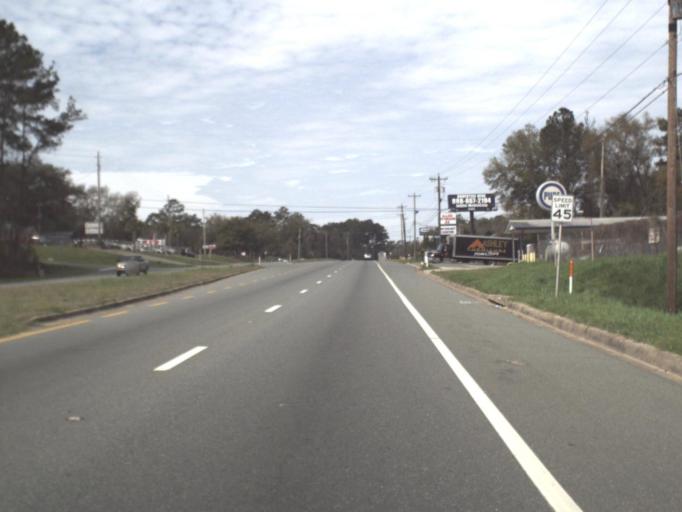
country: US
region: Florida
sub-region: Gadsden County
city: Midway
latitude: 30.4570
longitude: -84.3785
